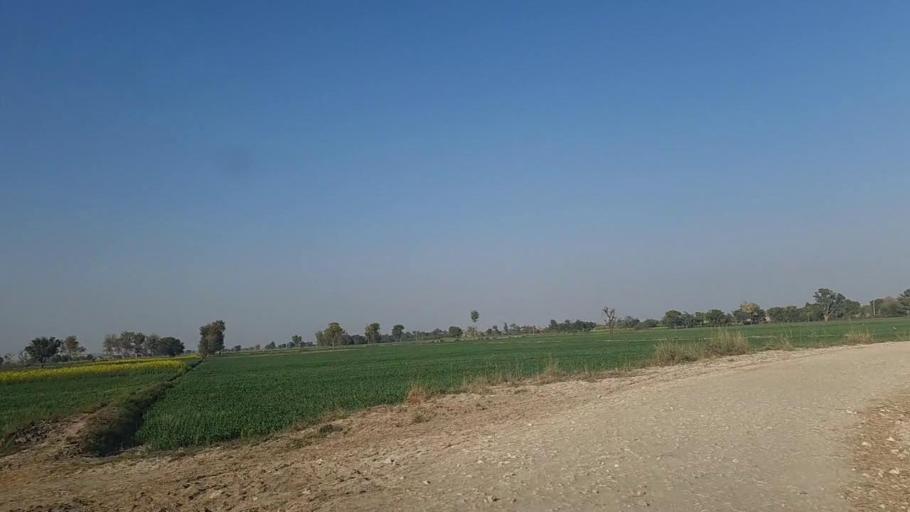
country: PK
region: Sindh
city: Jam Sahib
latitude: 26.3339
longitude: 68.7143
